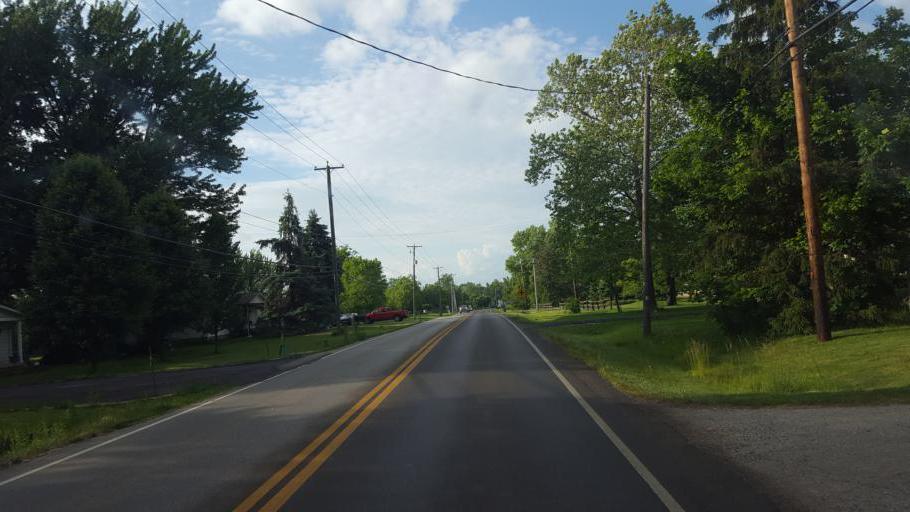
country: US
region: Ohio
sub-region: Delaware County
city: Lewis Center
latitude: 40.1930
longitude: -82.9909
